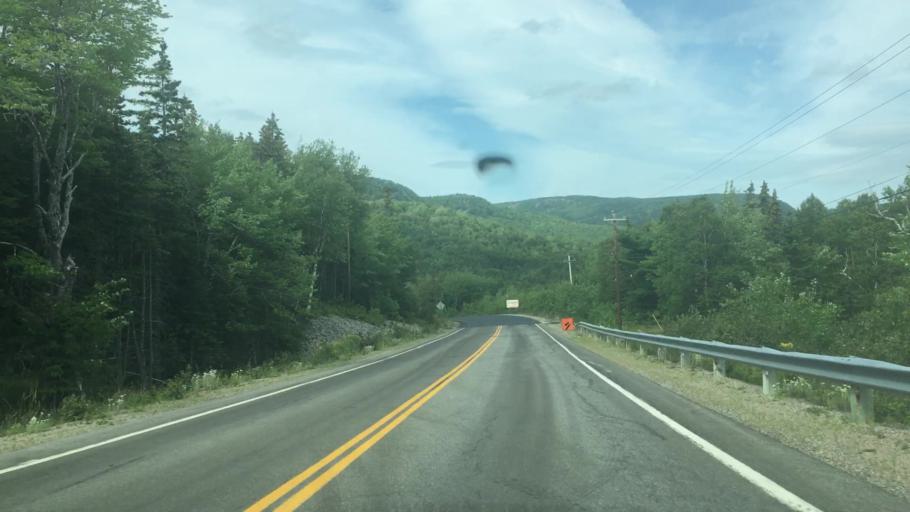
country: CA
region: Nova Scotia
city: Sydney Mines
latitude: 46.5419
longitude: -60.4141
